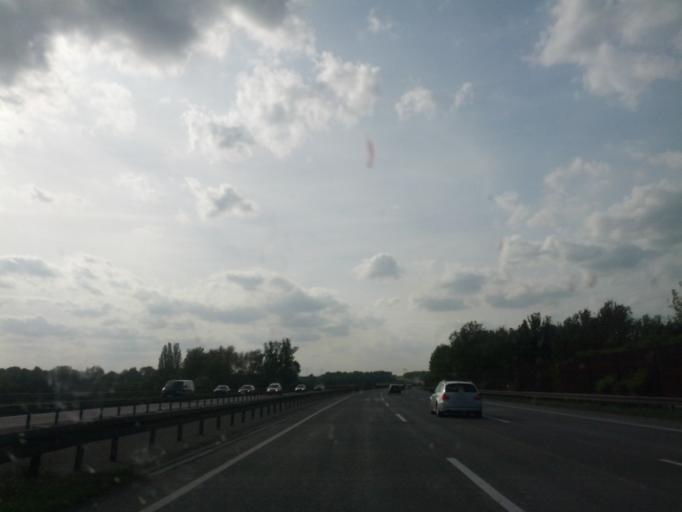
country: DE
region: Thuringia
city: Schwabhausen
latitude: 50.8883
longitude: 10.7669
